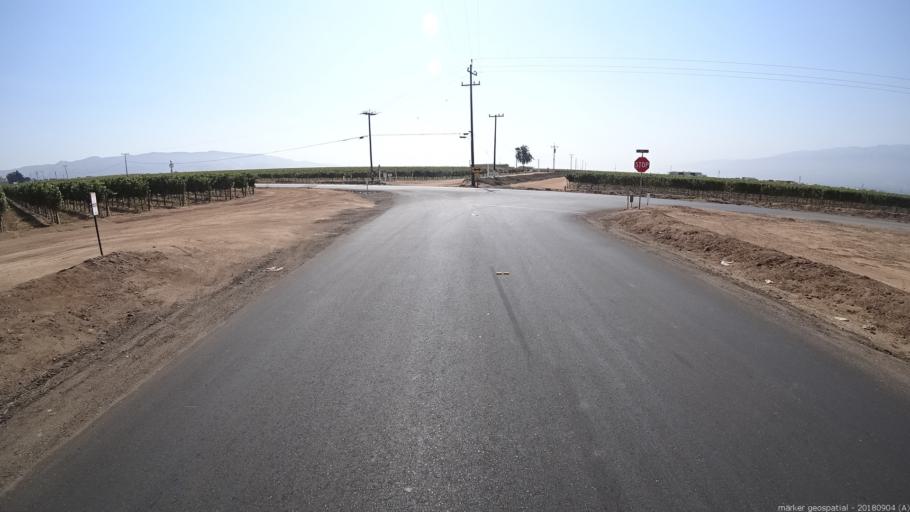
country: US
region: California
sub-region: Monterey County
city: Gonzales
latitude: 36.5010
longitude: -121.3971
